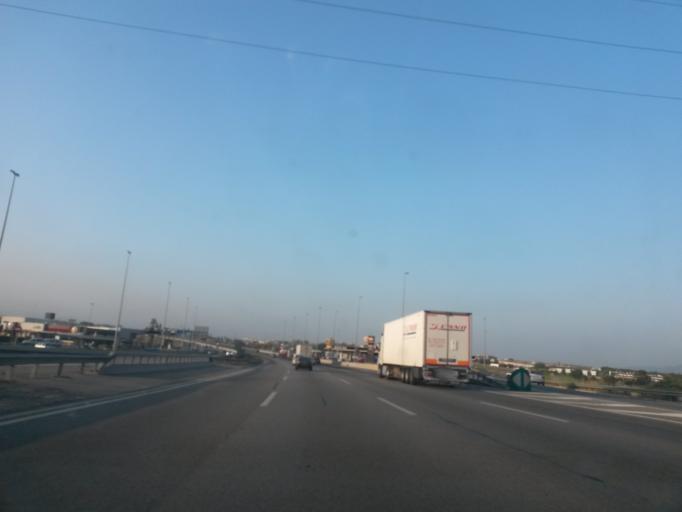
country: ES
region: Catalonia
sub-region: Provincia de Barcelona
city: Santa Perpetua de Mogoda
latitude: 41.5249
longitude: 2.1661
